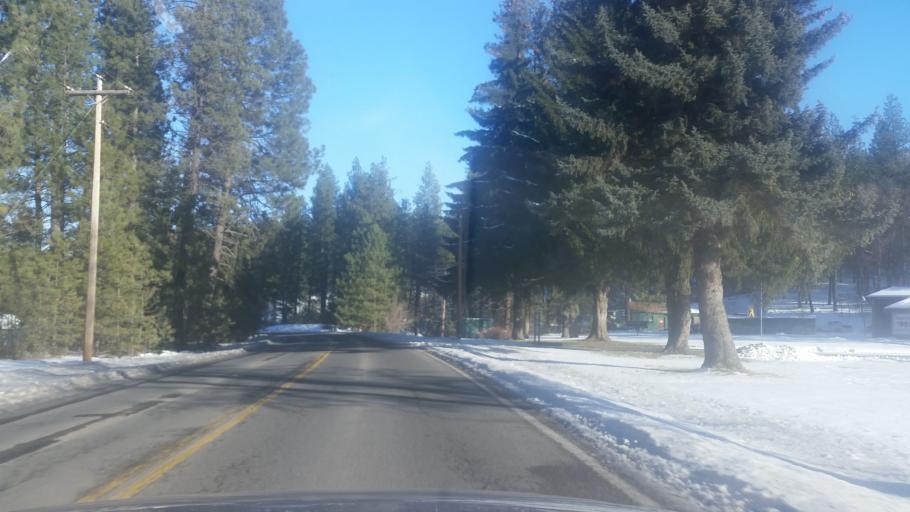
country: US
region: Washington
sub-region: Spokane County
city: Spokane
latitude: 47.6001
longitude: -117.4402
